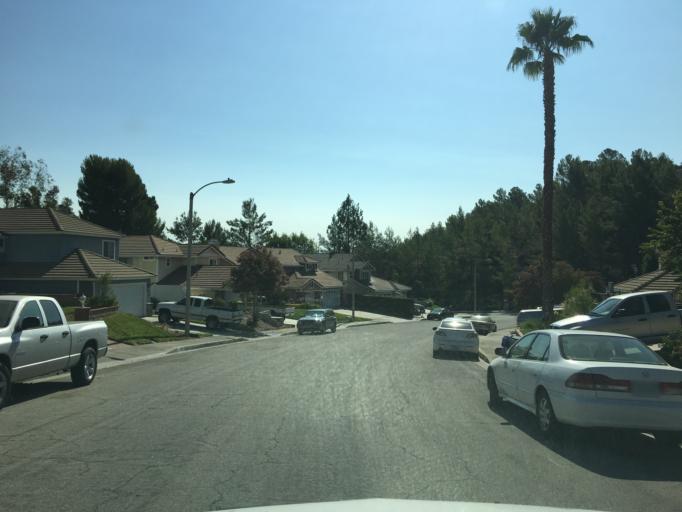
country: US
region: California
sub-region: Los Angeles County
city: Castaic
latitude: 34.4886
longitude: -118.6341
